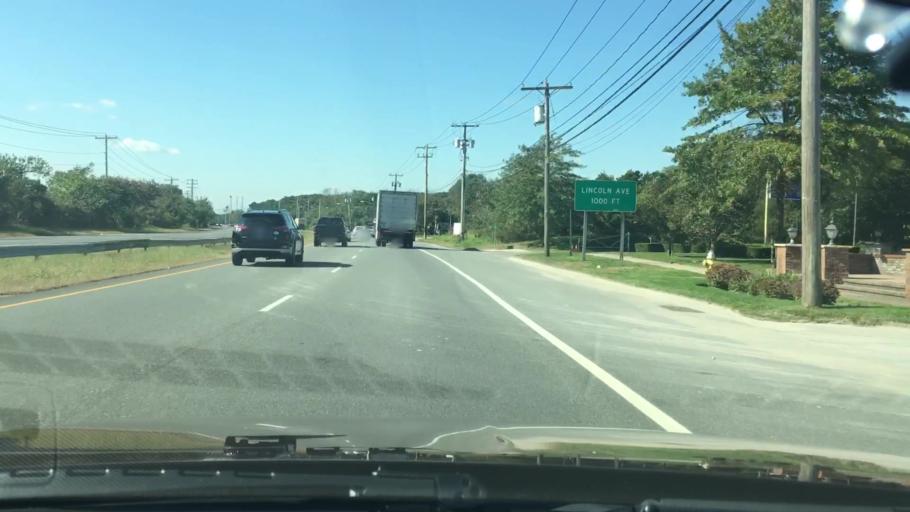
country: US
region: New York
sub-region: Suffolk County
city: Holbrook
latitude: 40.7812
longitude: -73.0801
